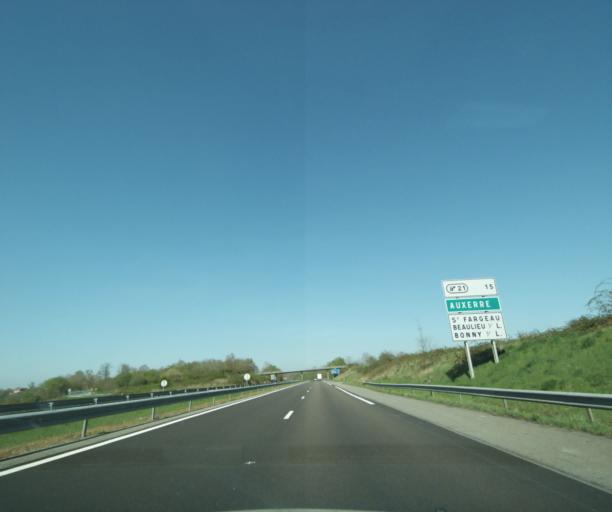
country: FR
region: Bourgogne
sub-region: Departement de la Nievre
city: Cosne-Cours-sur-Loire
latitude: 47.4414
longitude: 2.9438
